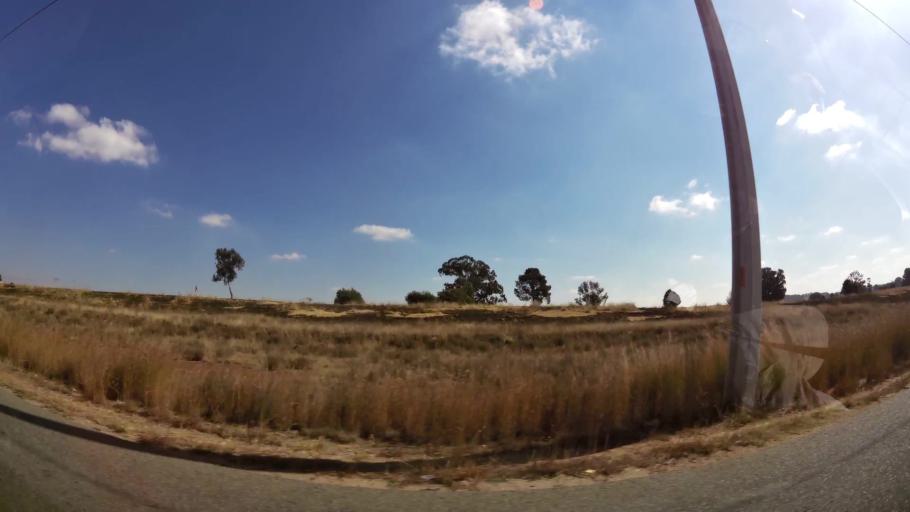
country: ZA
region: Gauteng
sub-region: West Rand District Municipality
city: Randfontein
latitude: -26.1593
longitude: 27.7620
